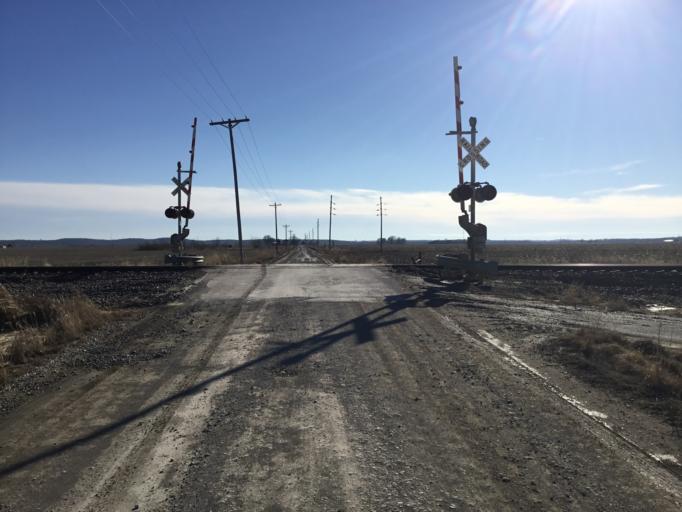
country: US
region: Kansas
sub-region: Shawnee County
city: Silver Lake
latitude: 39.1027
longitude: -95.8354
